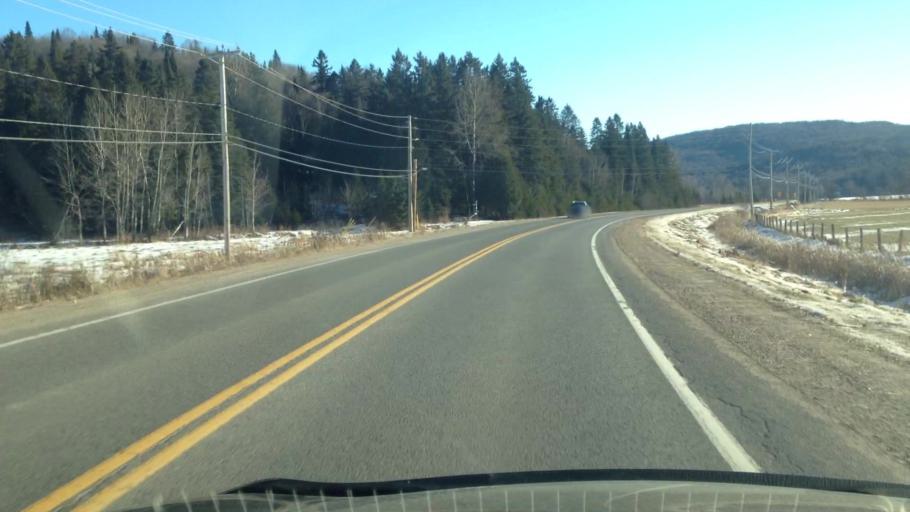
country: CA
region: Quebec
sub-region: Laurentides
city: Mont-Tremblant
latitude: 45.9566
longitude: -74.5668
